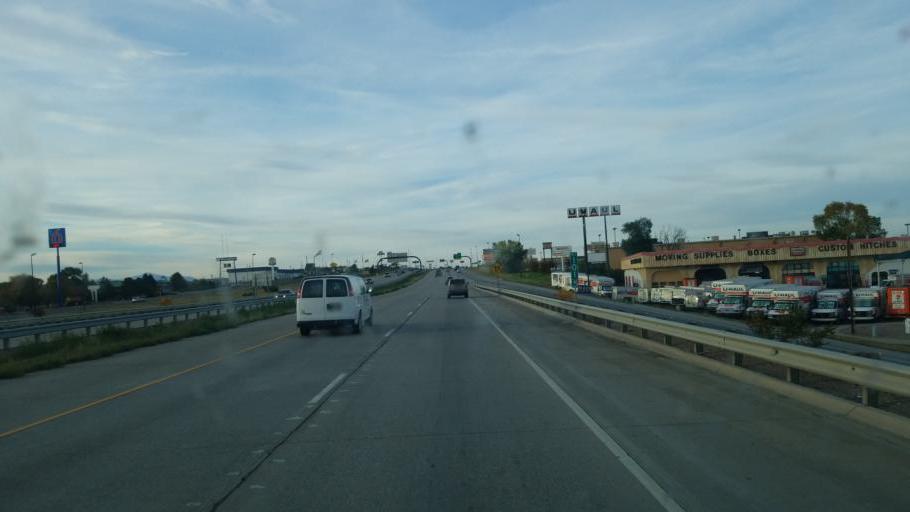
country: US
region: Colorado
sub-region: Pueblo County
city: Pueblo
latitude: 38.3088
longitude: -104.6139
